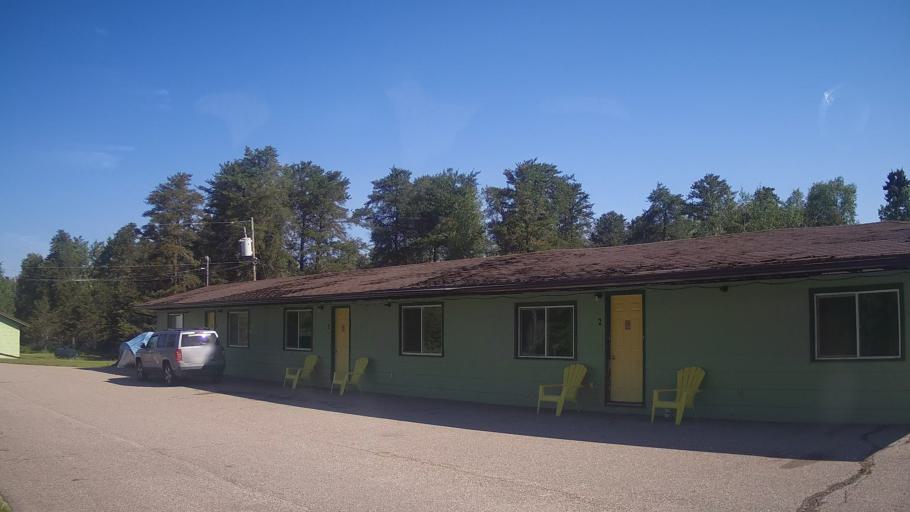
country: CA
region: Ontario
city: Dryden
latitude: 49.7331
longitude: -92.6116
